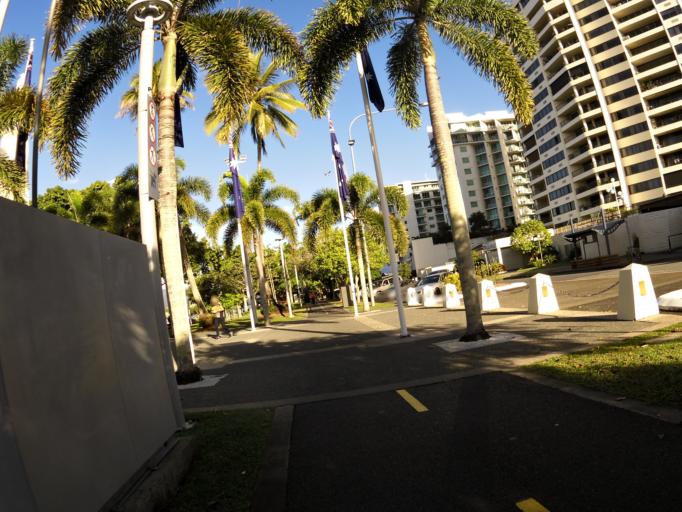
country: AU
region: Queensland
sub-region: Cairns
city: Cairns
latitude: -16.9174
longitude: 145.7753
